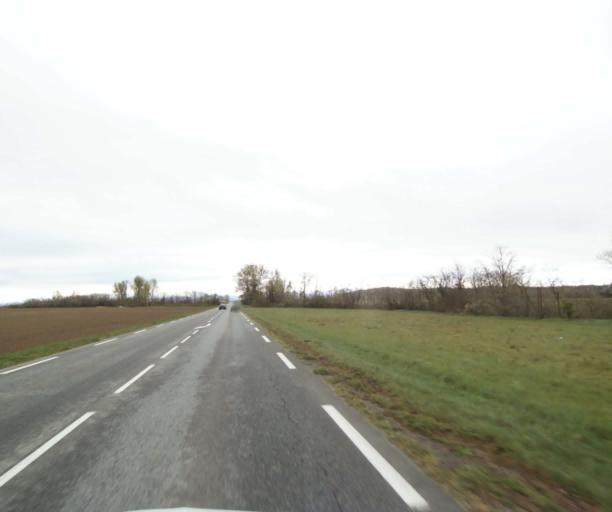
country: FR
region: Midi-Pyrenees
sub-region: Departement de l'Ariege
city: Saverdun
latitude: 43.2214
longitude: 1.6068
